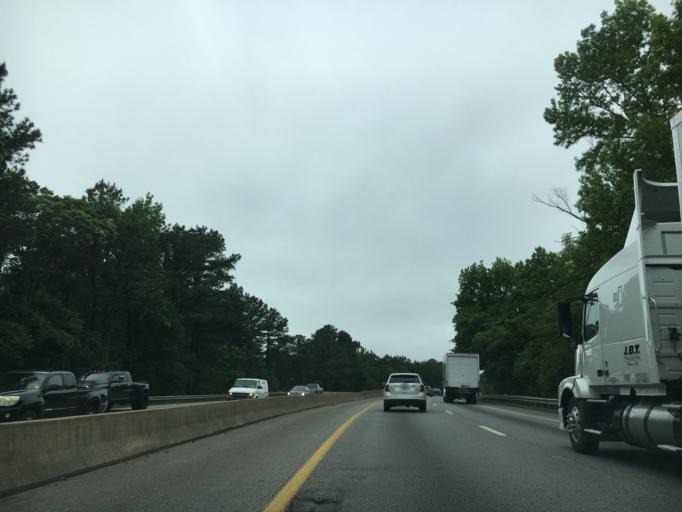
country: US
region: Virginia
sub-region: City of Petersburg
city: Petersburg
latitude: 37.1992
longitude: -77.4186
